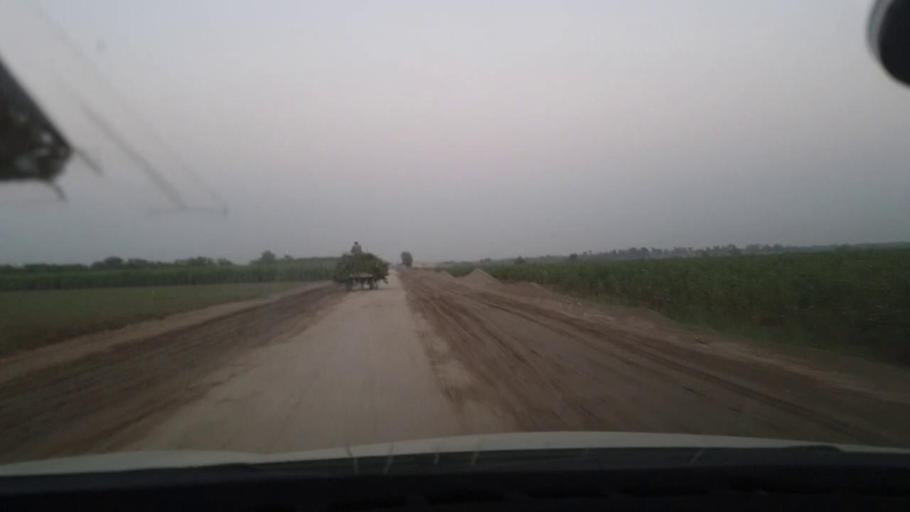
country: PK
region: Sindh
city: Tando Adam
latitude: 25.7559
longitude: 68.6221
